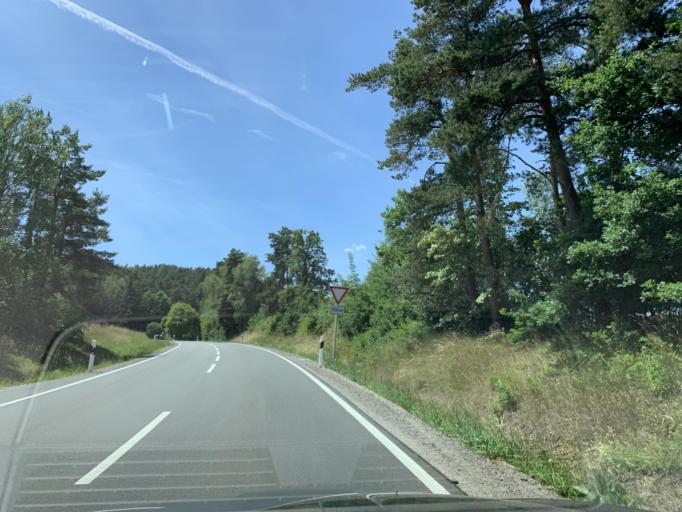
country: DE
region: Bavaria
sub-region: Upper Palatinate
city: Pettendorf
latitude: 49.3430
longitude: 12.3633
